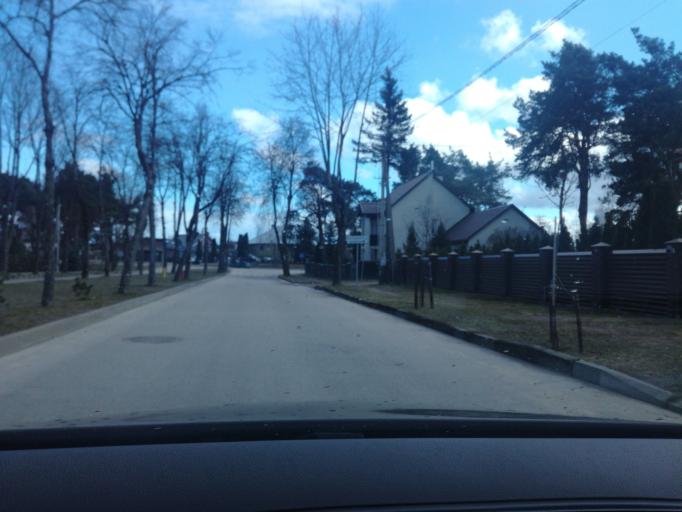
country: LT
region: Alytaus apskritis
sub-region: Alytus
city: Alytus
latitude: 54.3896
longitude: 24.0503
